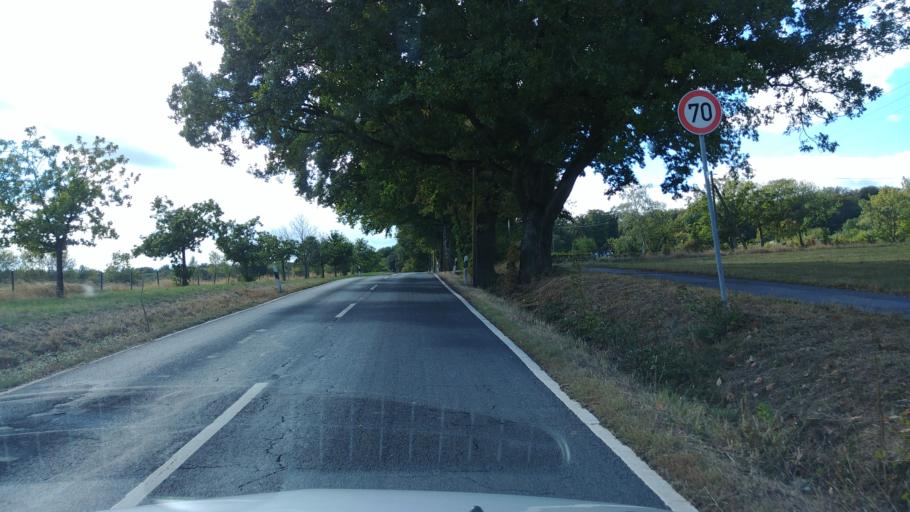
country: DE
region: Hesse
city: Taunusstein
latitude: 50.1012
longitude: 8.1902
